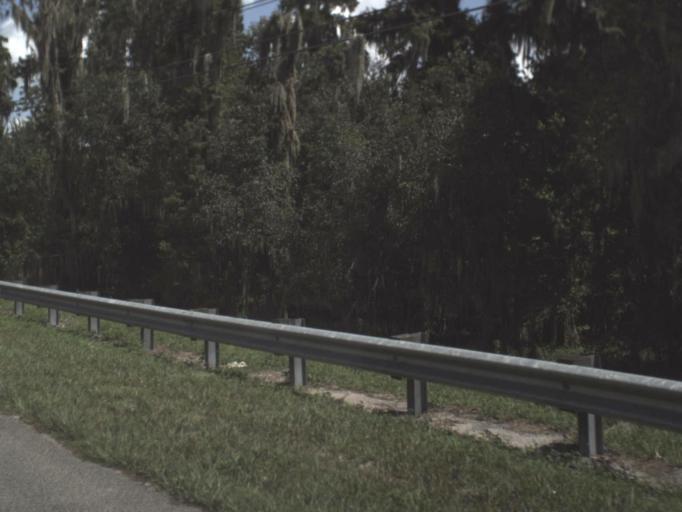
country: US
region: Florida
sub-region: Polk County
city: Bartow
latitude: 27.9174
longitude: -81.8250
